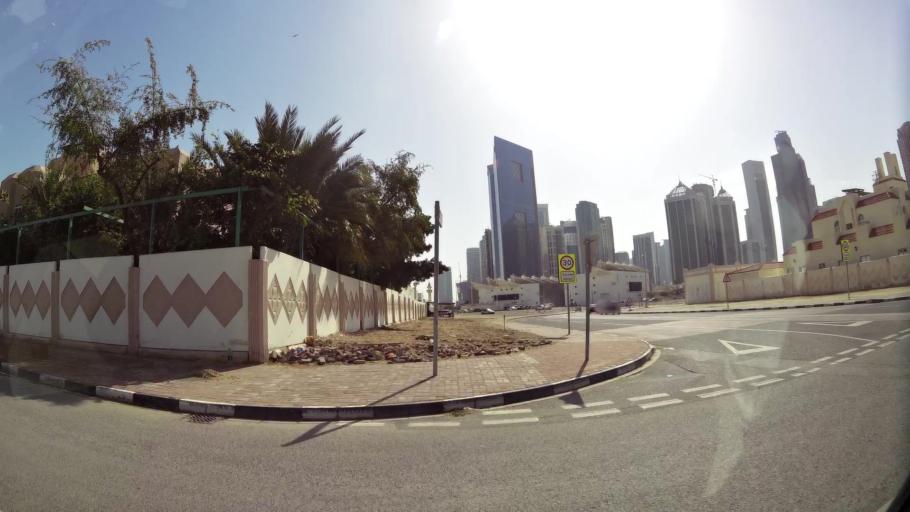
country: QA
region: Baladiyat ad Dawhah
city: Doha
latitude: 25.3309
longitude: 51.5201
